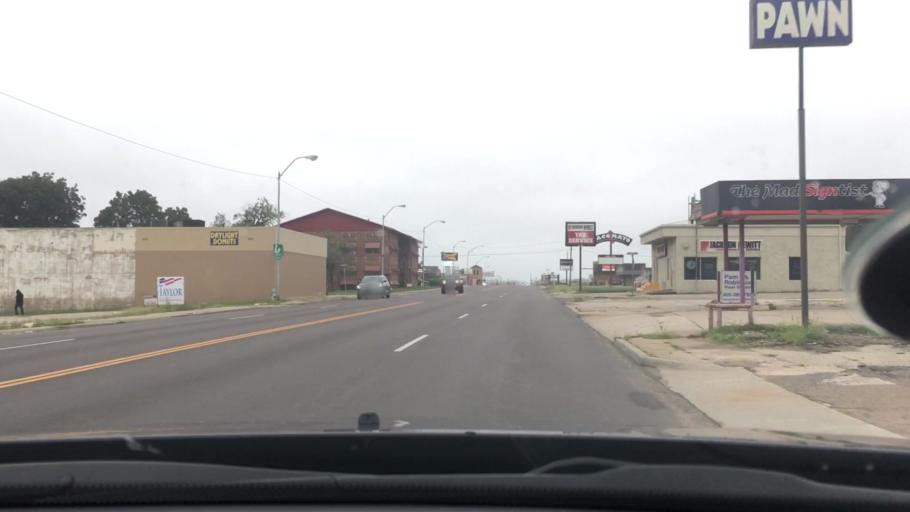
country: US
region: Oklahoma
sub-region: Seminole County
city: Seminole
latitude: 35.2269
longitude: -96.6710
